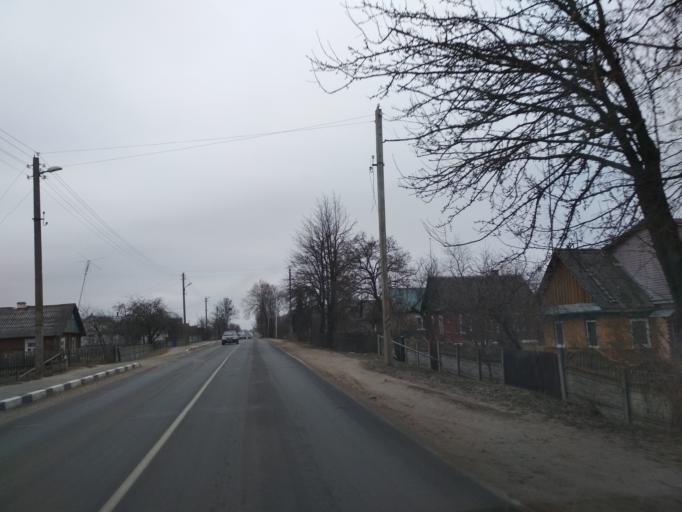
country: BY
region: Minsk
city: Mar''ina Horka
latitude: 53.4989
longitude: 28.1477
